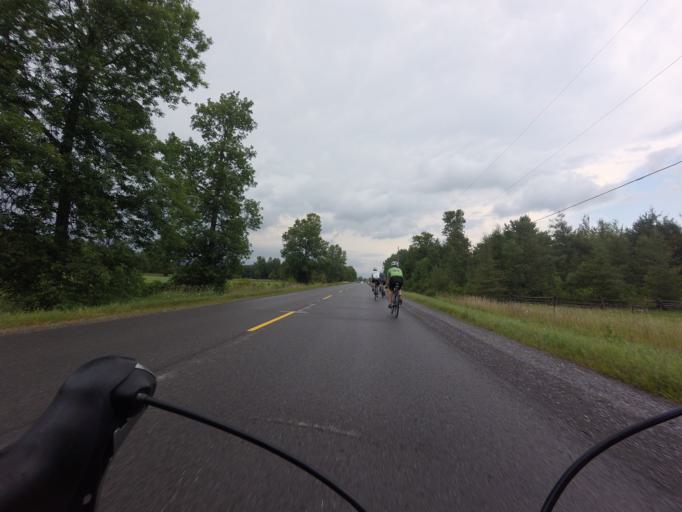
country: CA
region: Ontario
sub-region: Lanark County
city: Smiths Falls
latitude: 44.8436
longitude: -75.8161
